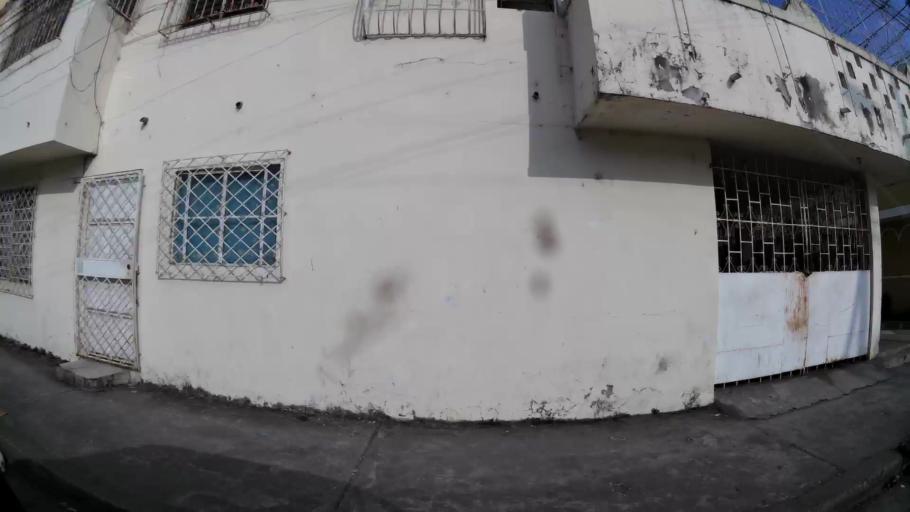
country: EC
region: Guayas
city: Eloy Alfaro
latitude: -2.1354
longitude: -79.8897
